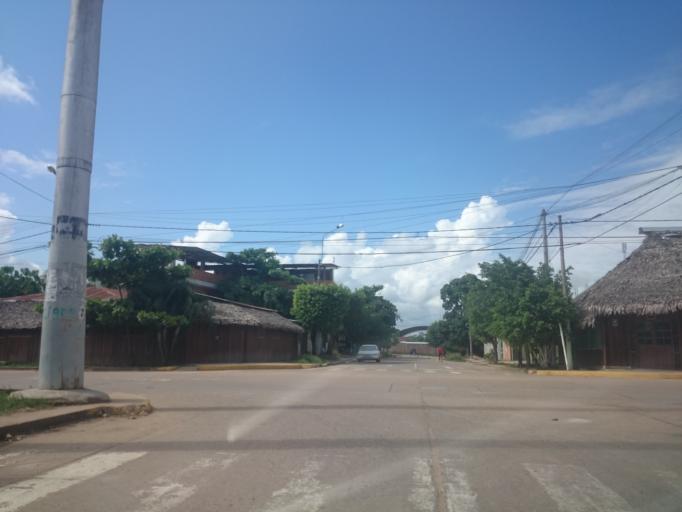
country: PE
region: Ucayali
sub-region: Provincia de Coronel Portillo
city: Puerto Callao
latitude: -8.3549
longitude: -74.5779
